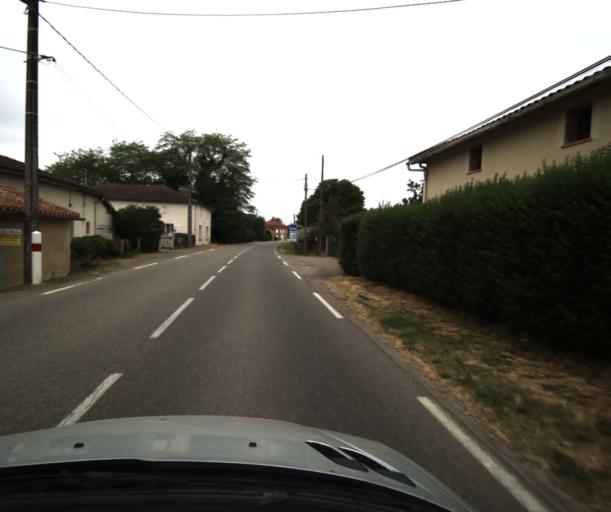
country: FR
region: Midi-Pyrenees
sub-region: Departement du Tarn-et-Garonne
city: Saint-Nicolas-de-la-Grave
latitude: 44.0697
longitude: 1.0078
